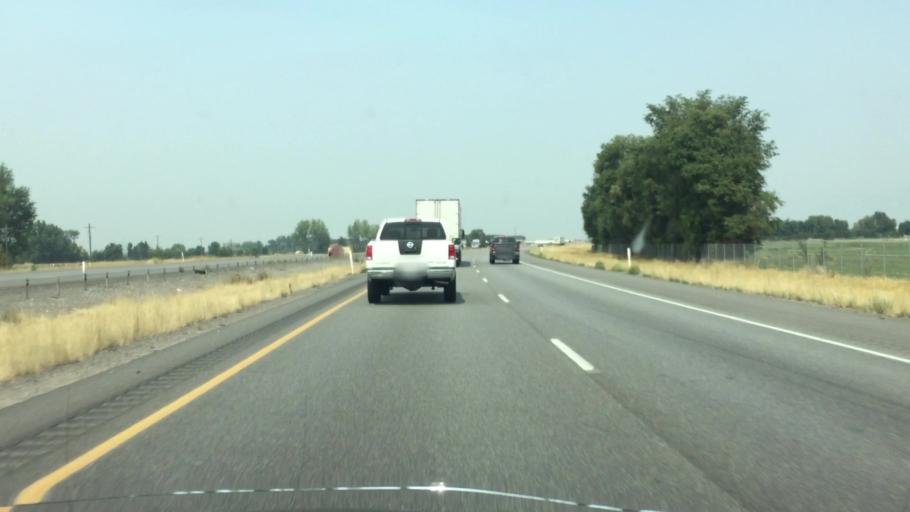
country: US
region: Utah
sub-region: Utah County
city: Payson
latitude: 40.0213
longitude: -111.7622
